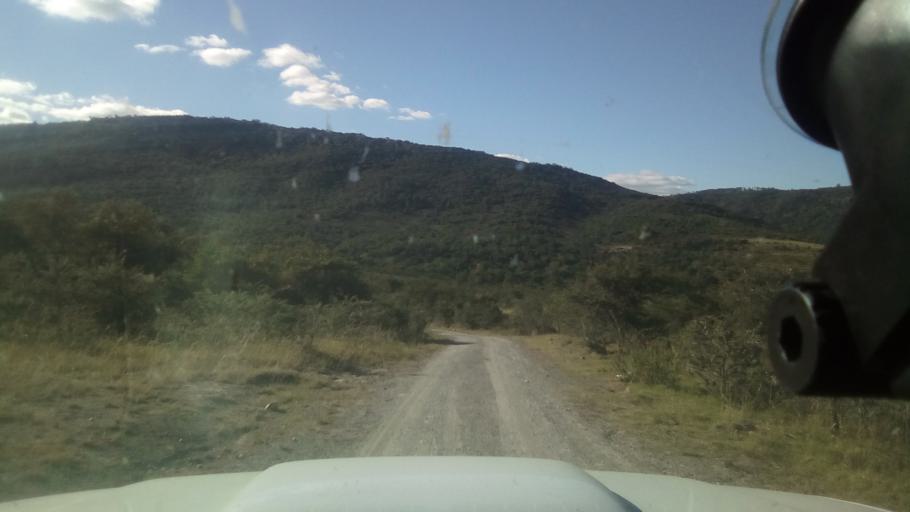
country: ZA
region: Eastern Cape
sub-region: Buffalo City Metropolitan Municipality
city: Bhisho
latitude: -32.7303
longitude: 27.3484
